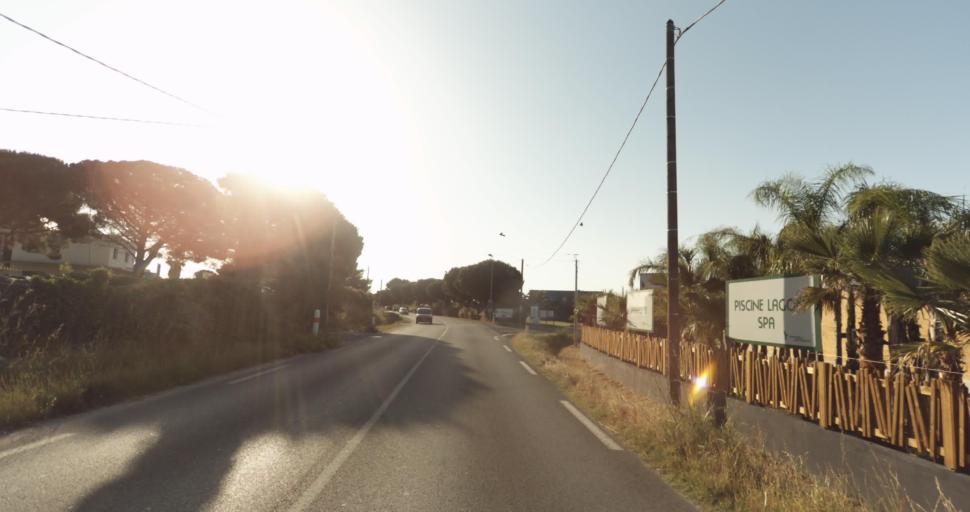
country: FR
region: Languedoc-Roussillon
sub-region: Departement des Pyrenees-Orientales
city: Latour-Bas-Elne
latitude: 42.6069
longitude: 2.9926
